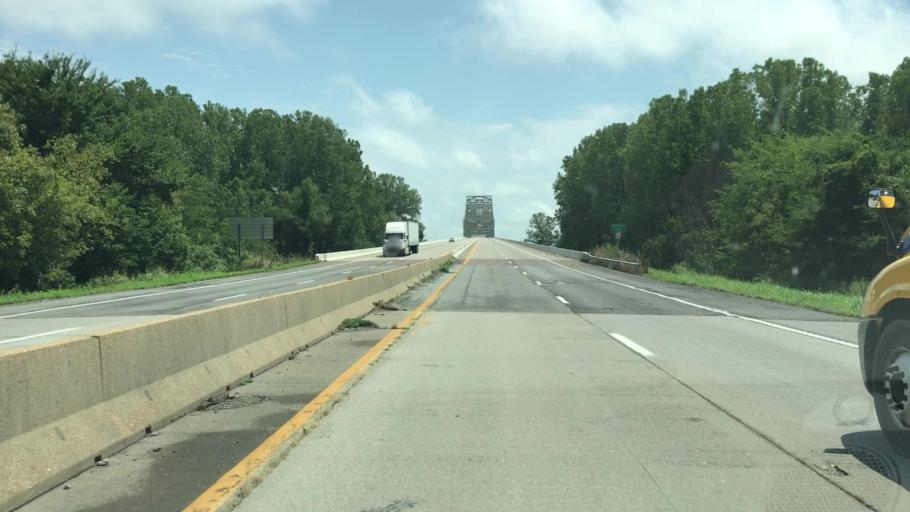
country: US
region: Missouri
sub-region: Pemiscot County
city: Caruthersville
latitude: 36.1213
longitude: -89.6168
